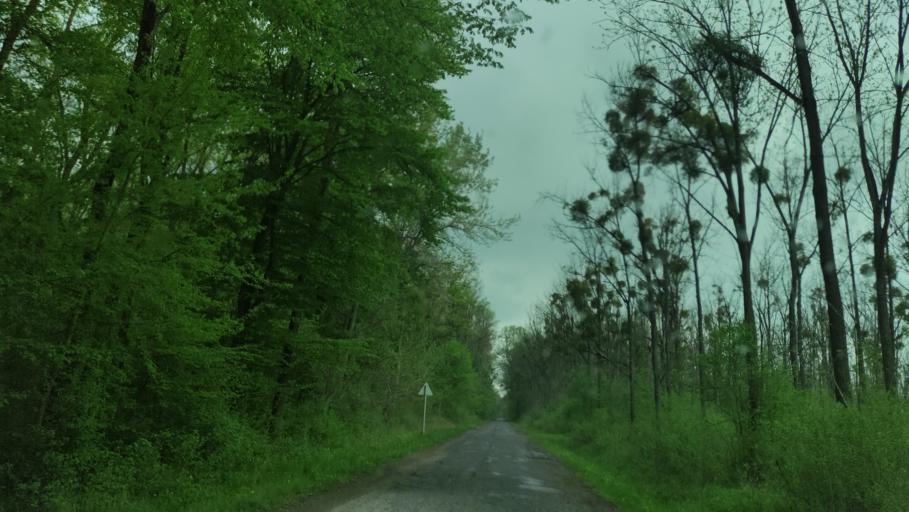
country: HU
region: Baranya
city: Mohacs
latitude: 45.9244
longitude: 18.7278
